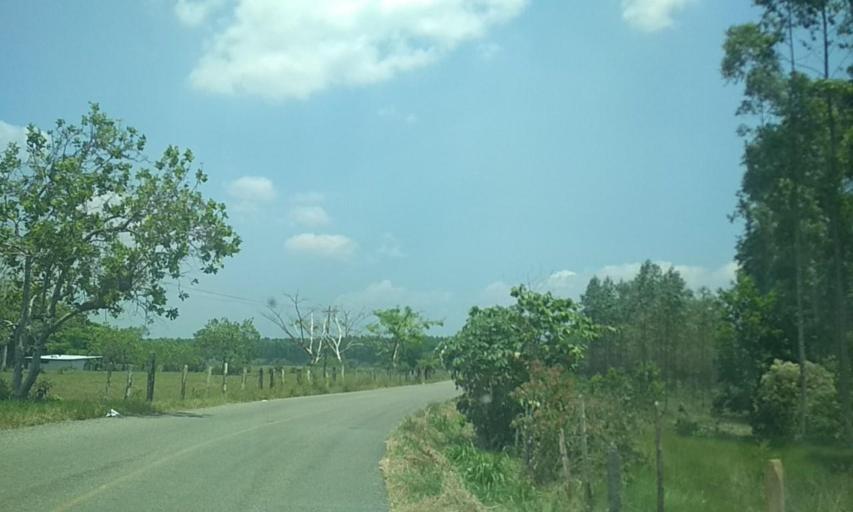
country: MX
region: Tabasco
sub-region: Huimanguillo
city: Francisco Rueda
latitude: 17.8385
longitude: -93.9094
